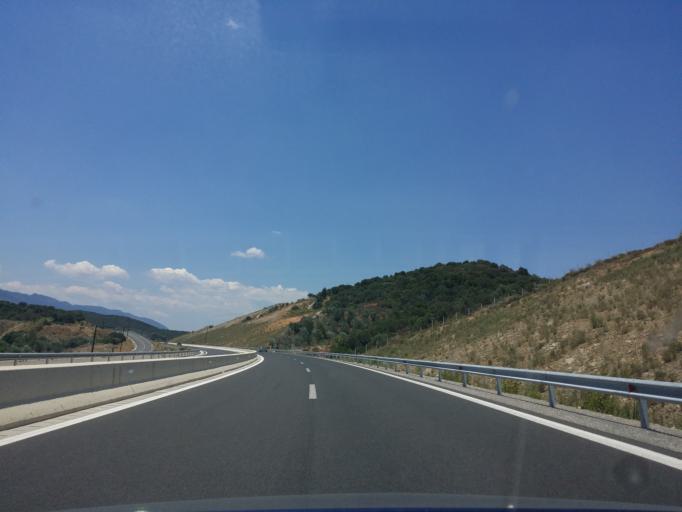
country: GR
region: Peloponnese
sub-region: Nomos Lakonias
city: Magoula
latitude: 37.1357
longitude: 22.3976
